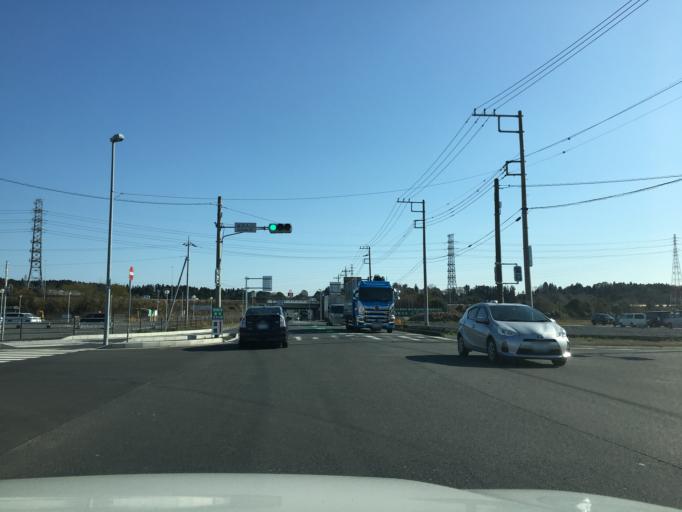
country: JP
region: Ibaraki
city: Mito-shi
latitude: 36.4189
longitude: 140.4240
